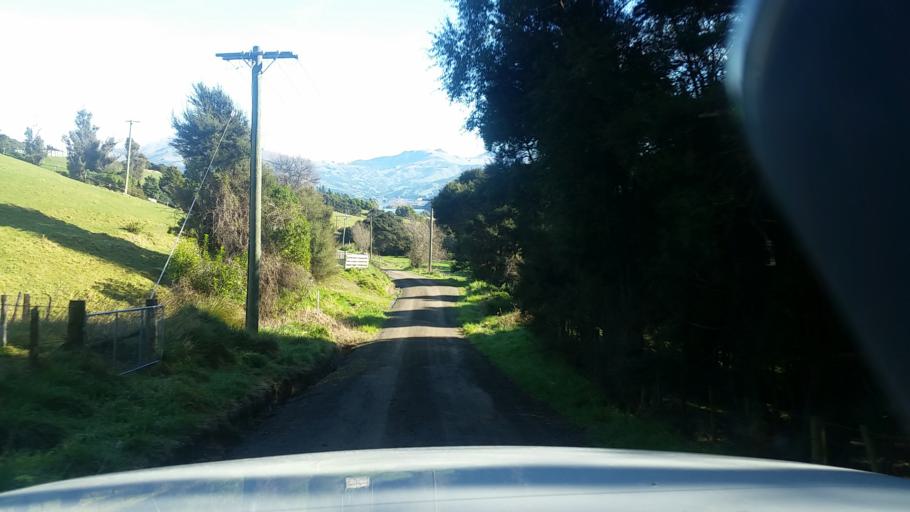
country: NZ
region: Canterbury
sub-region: Christchurch City
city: Christchurch
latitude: -43.7907
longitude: 172.9888
